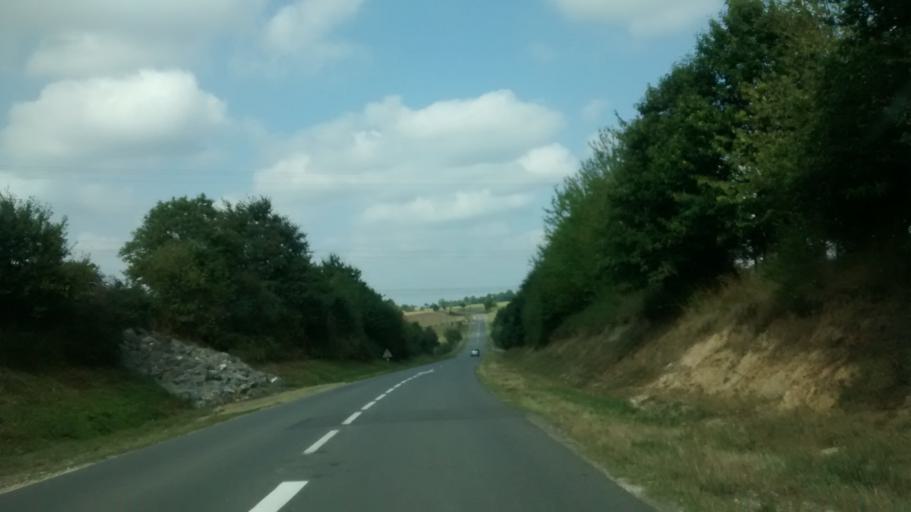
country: FR
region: Brittany
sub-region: Departement d'Ille-et-Vilaine
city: Livre-sur-Changeon
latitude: 48.2264
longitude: -1.3523
